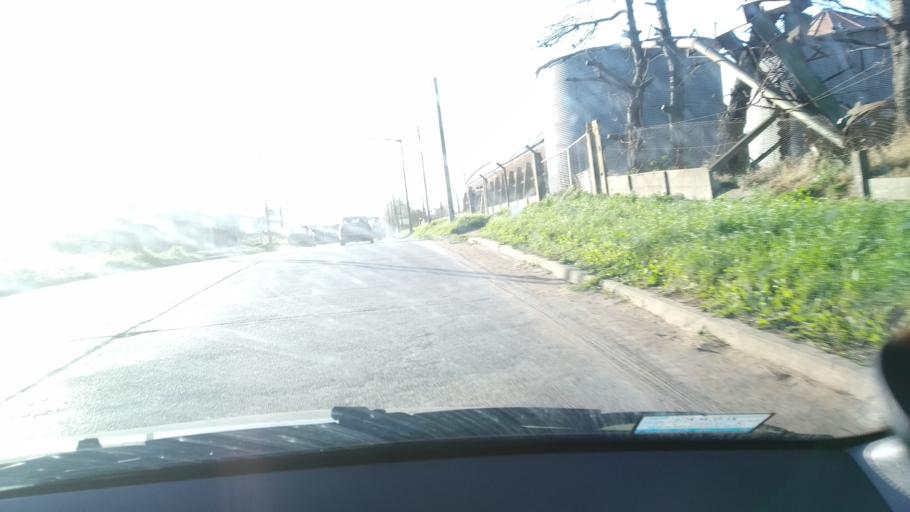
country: AR
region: Buenos Aires
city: Necochea
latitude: -38.5637
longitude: -58.7084
